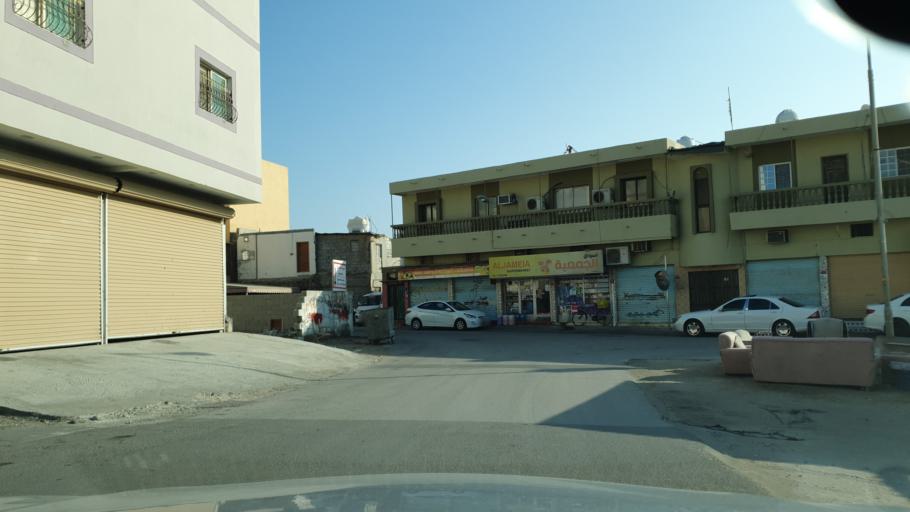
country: BH
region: Manama
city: Jidd Hafs
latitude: 26.2187
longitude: 50.4639
